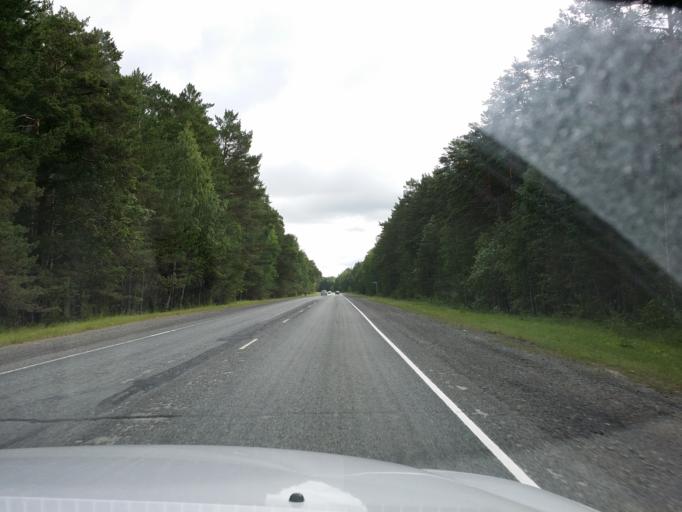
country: RU
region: Tjumen
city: Yalutorovsk
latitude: 57.1599
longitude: 66.5292
